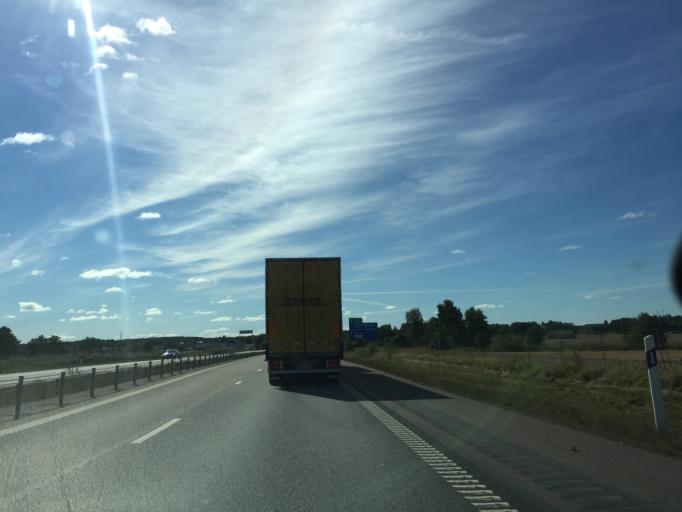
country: SE
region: Vaestmanland
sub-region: Kopings Kommun
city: Koping
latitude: 59.5290
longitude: 15.9801
